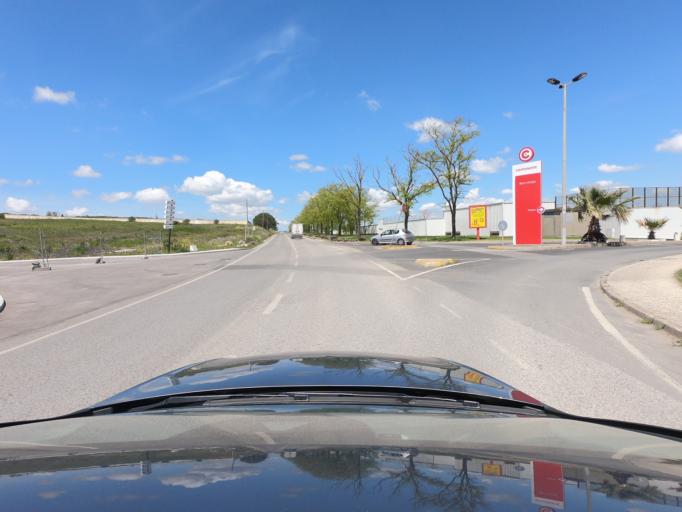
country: PT
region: Lisbon
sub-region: Amadora
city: Amadora
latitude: 38.7399
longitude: -9.2331
